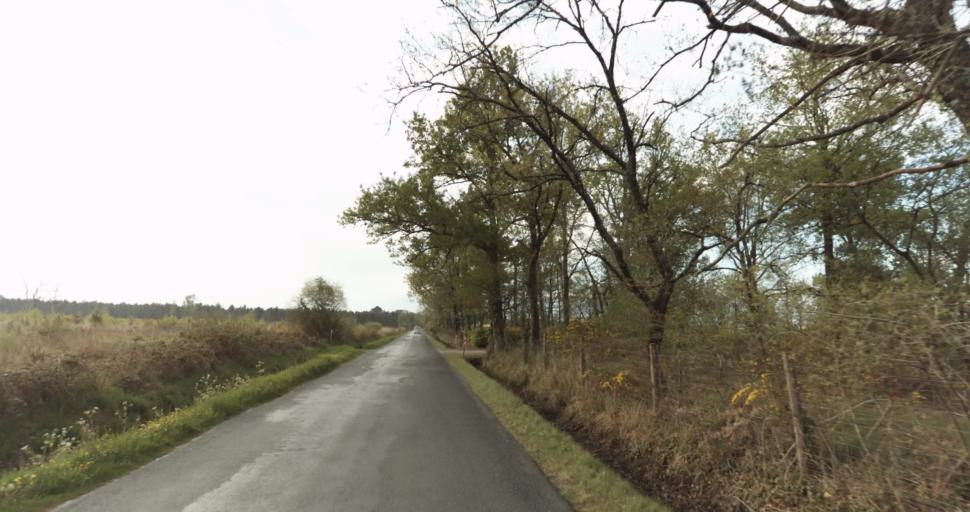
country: FR
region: Aquitaine
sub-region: Departement de la Gironde
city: Saint-Aubin-de-Medoc
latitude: 44.7794
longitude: -0.7447
